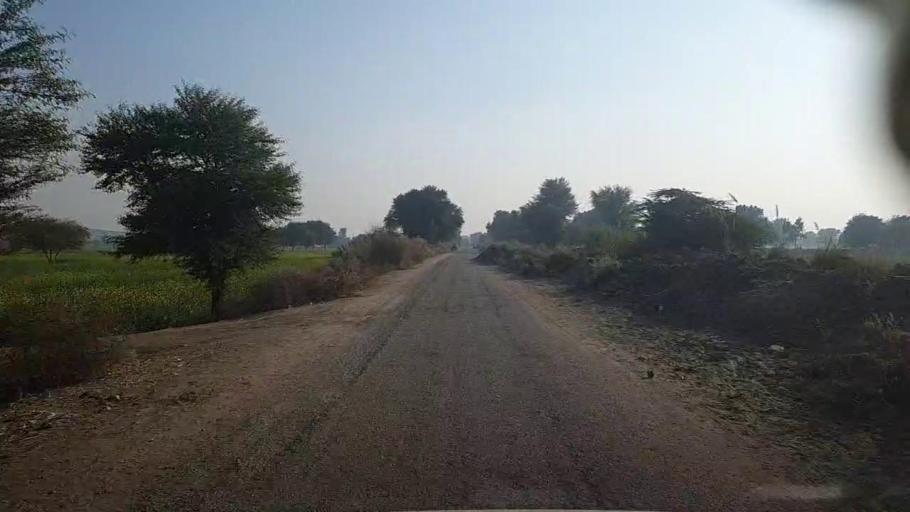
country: PK
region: Sindh
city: Karaundi
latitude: 26.7560
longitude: 68.4766
